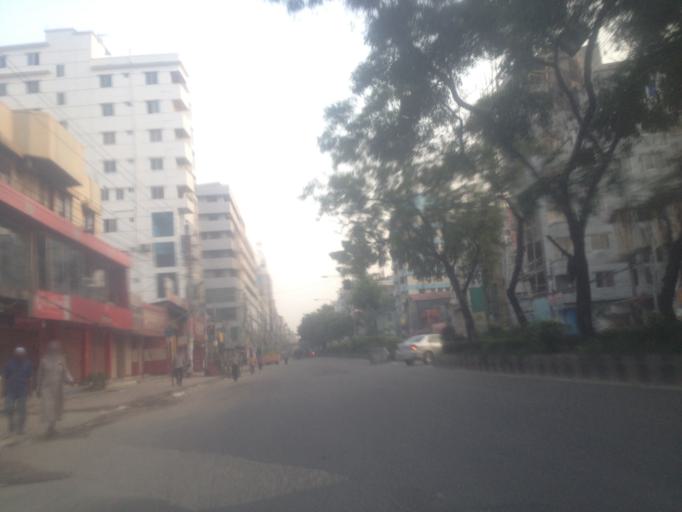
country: BD
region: Dhaka
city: Azimpur
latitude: 23.7885
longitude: 90.3765
